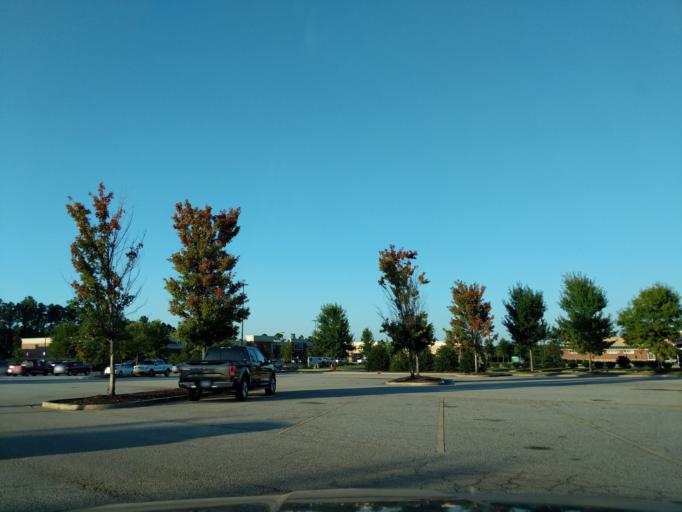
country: US
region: Georgia
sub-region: Columbia County
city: Grovetown
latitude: 33.4801
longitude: -82.1950
